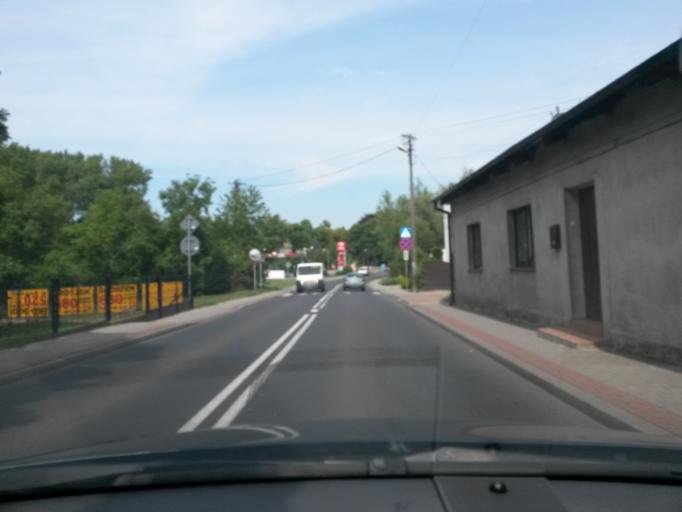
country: PL
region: Greater Poland Voivodeship
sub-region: Powiat sremski
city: Dolsk
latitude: 51.9875
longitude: 17.0662
